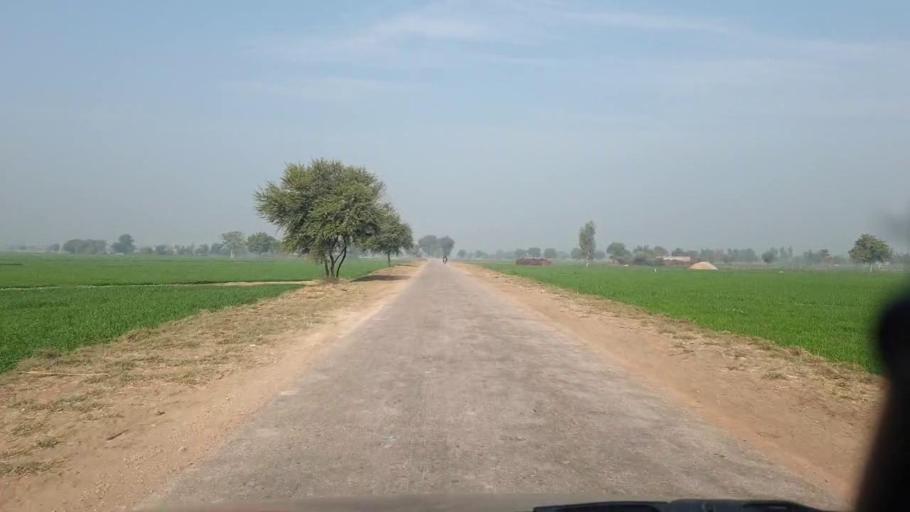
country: PK
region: Sindh
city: Shahdadpur
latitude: 26.0044
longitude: 68.5528
